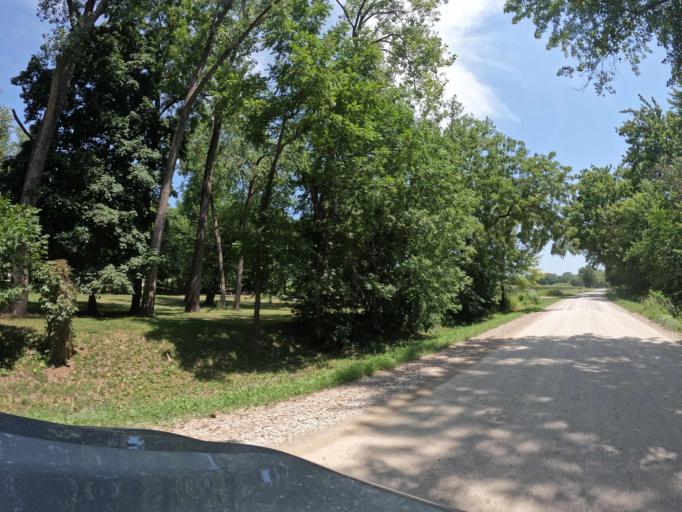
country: US
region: Iowa
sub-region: Henry County
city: Mount Pleasant
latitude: 40.9335
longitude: -91.6083
